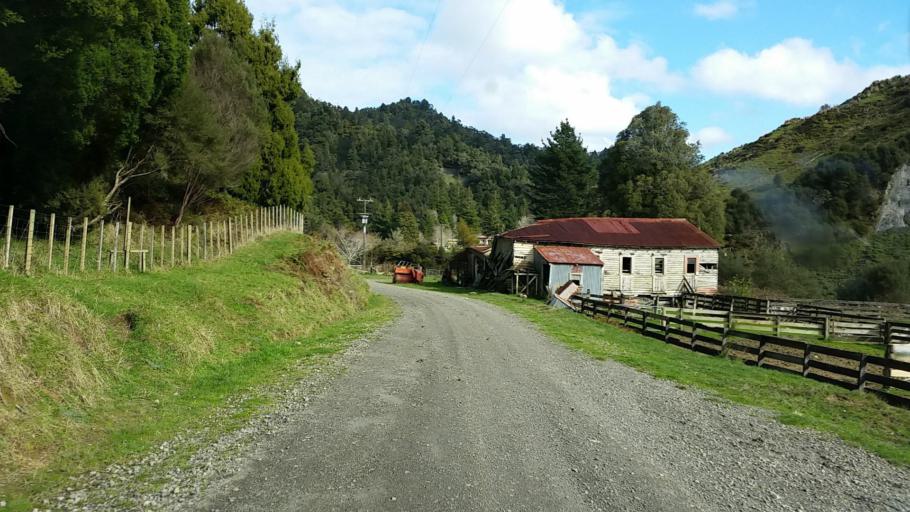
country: NZ
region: Taranaki
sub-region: New Plymouth District
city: Waitara
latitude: -39.0970
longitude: 174.5648
